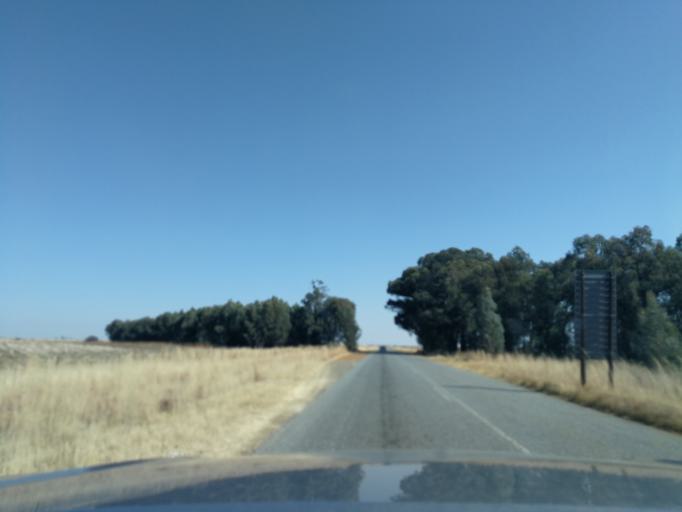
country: ZA
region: North-West
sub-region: Dr Kenneth Kaunda District Municipality
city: Orkney
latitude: -27.0515
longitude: 26.7240
